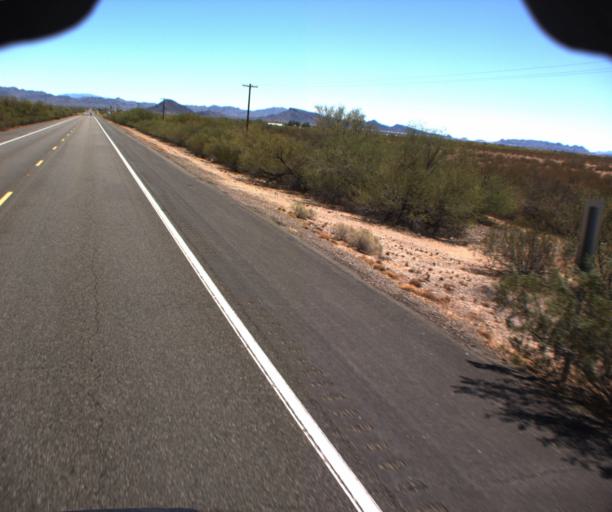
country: US
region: Arizona
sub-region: La Paz County
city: Salome
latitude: 33.7063
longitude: -113.8282
